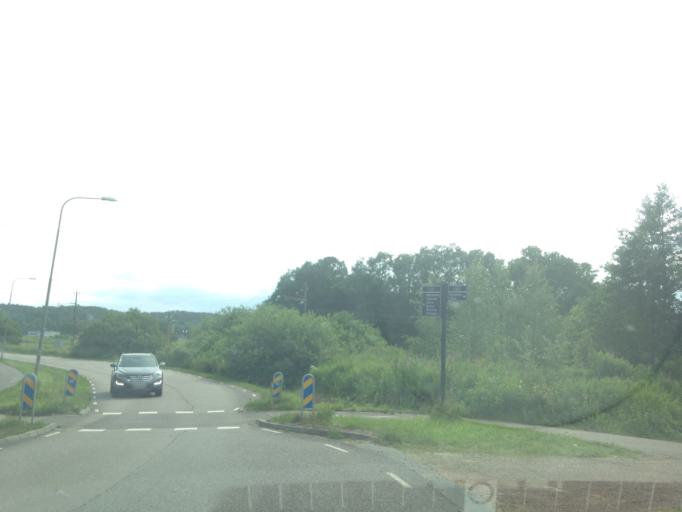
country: SE
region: Vaestra Goetaland
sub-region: Goteborg
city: Goeteborg
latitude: 57.7608
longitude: 11.9459
